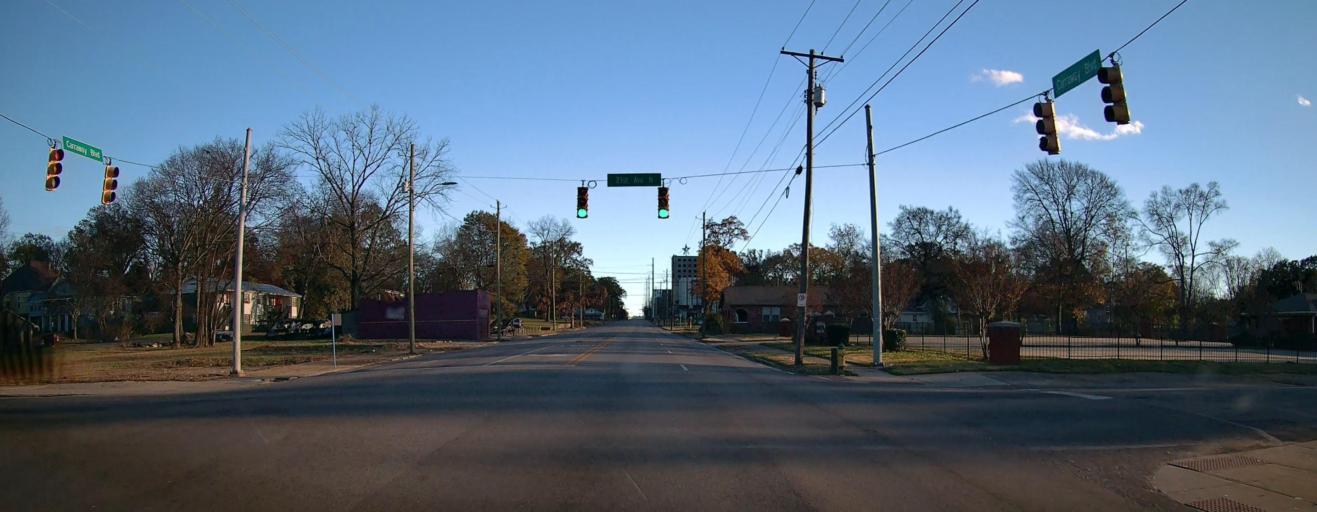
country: US
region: Alabama
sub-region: Jefferson County
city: Birmingham
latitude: 33.5417
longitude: -86.8132
